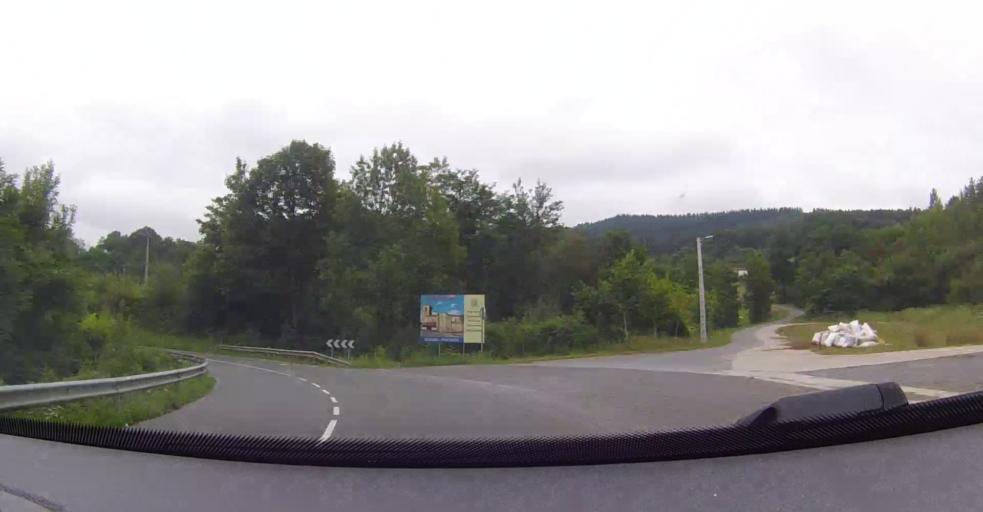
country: ES
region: Basque Country
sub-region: Bizkaia
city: Balmaseda
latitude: 43.2427
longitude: -3.2543
